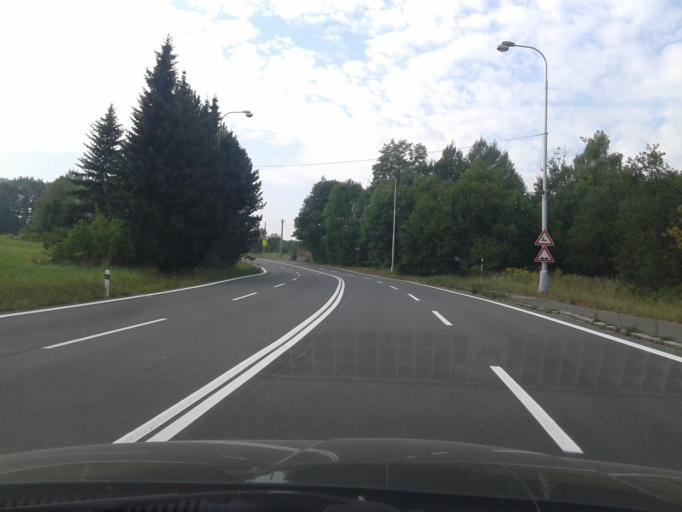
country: CZ
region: Moravskoslezsky
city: Orlova
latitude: 49.8383
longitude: 18.4349
